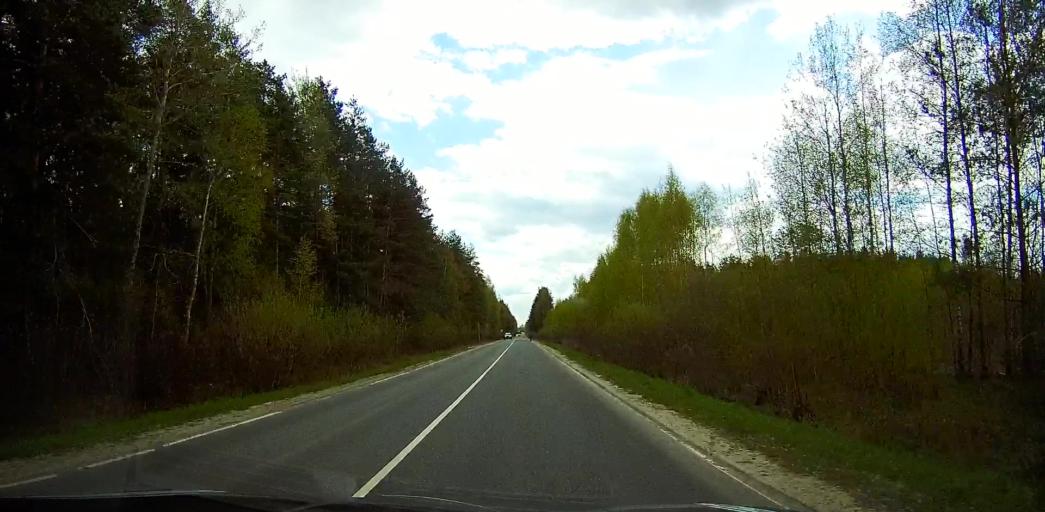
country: RU
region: Moskovskaya
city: Davydovo
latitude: 55.6582
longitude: 38.7541
